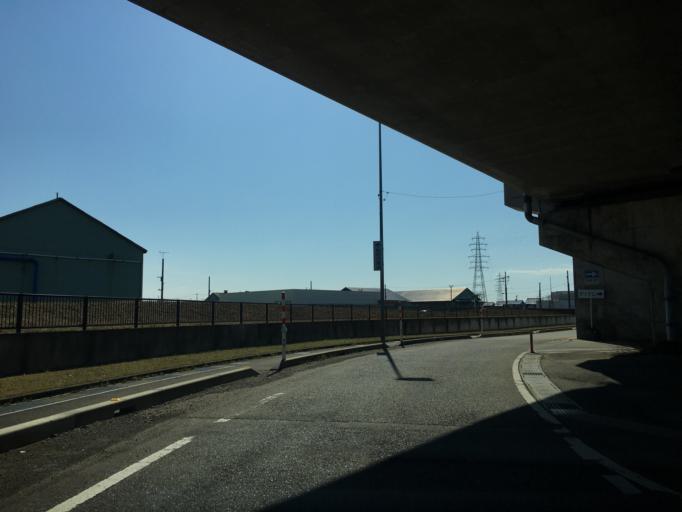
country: JP
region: Toyama
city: Nishishinminato
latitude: 36.7734
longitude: 137.0529
